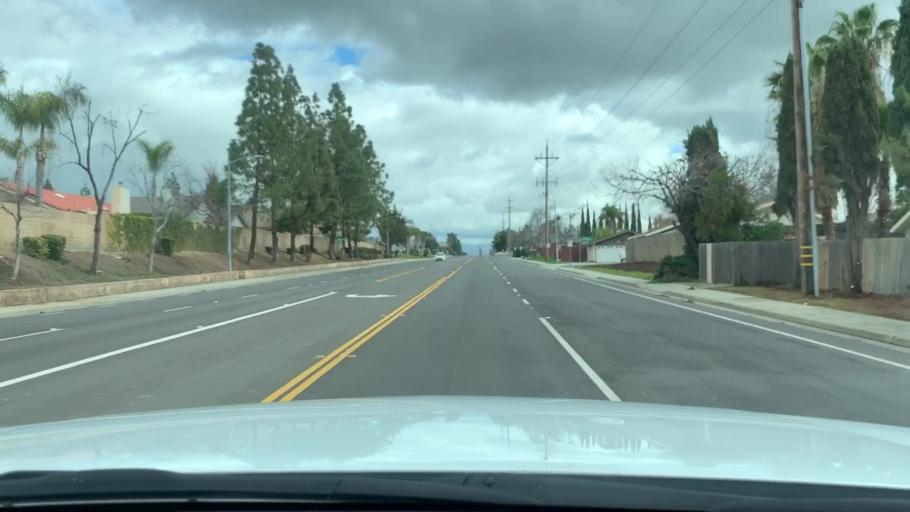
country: US
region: California
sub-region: Kern County
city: Bakersfield
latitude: 35.3978
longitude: -118.9385
